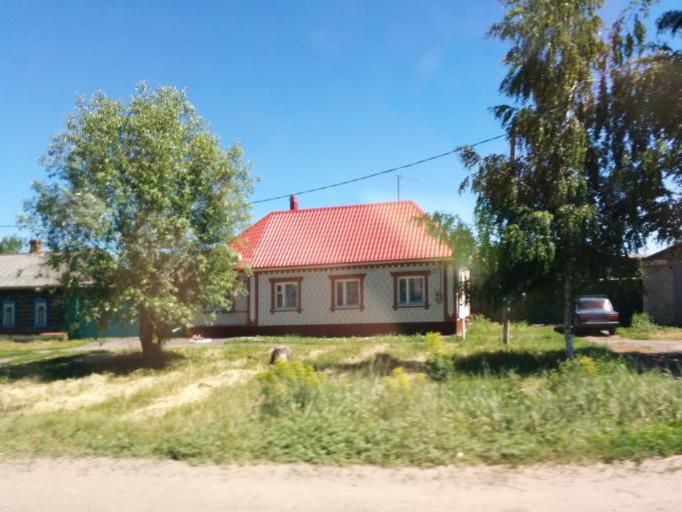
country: RU
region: Tambov
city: Morshansk
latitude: 53.3955
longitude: 41.7850
